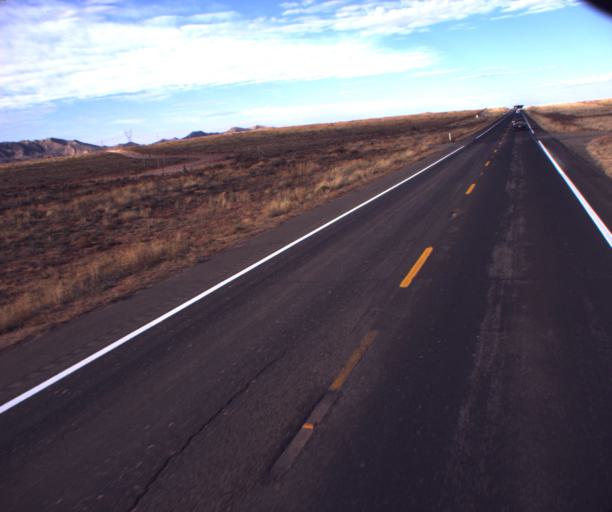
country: US
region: Arizona
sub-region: Apache County
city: Lukachukai
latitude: 36.9612
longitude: -109.3942
